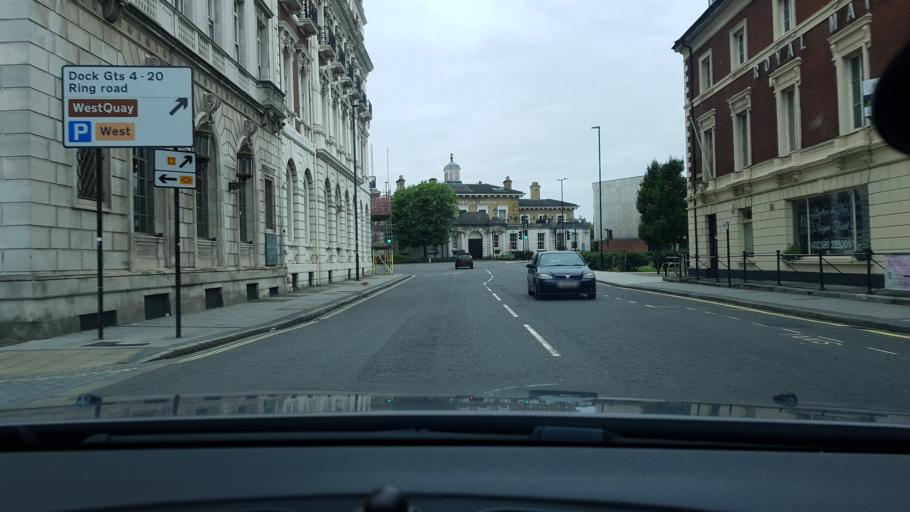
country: GB
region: England
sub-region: Southampton
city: Southampton
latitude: 50.8978
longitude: -1.3970
